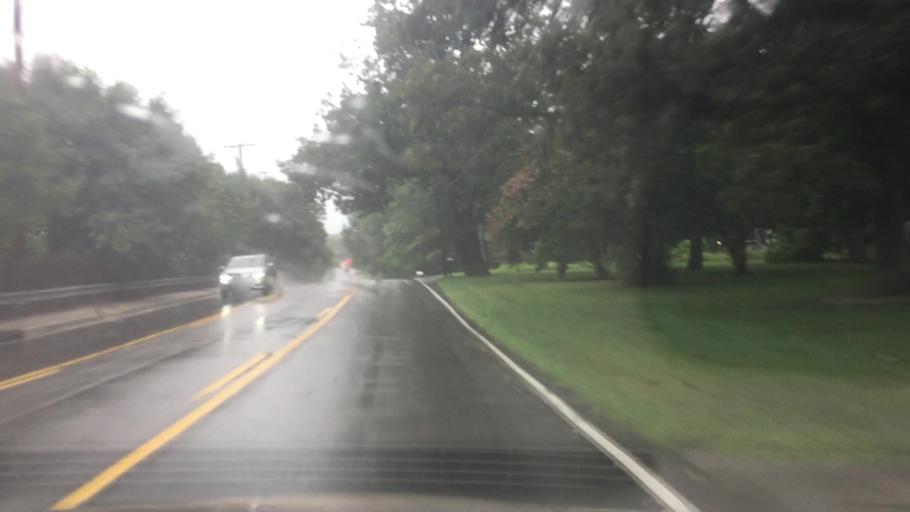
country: US
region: Maryland
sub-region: Anne Arundel County
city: Severn
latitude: 39.1367
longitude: -76.7174
